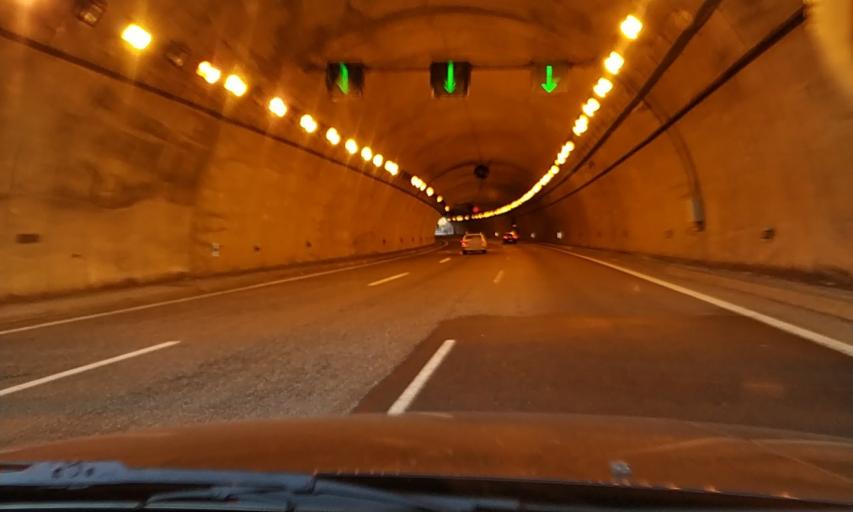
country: ES
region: Castille and Leon
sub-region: Provincia de Leon
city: Balboa
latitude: 42.7357
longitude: -7.0468
